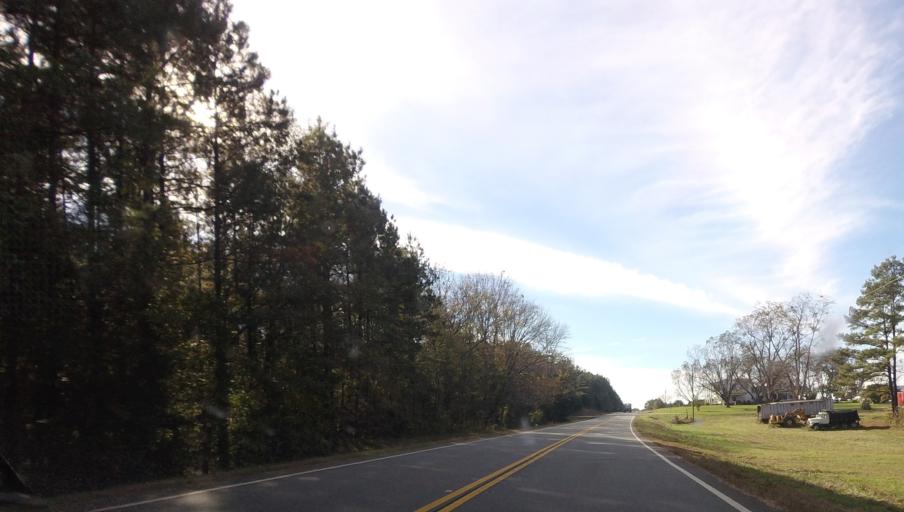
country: US
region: Georgia
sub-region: Talbot County
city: Talbotton
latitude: 32.7048
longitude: -84.3977
